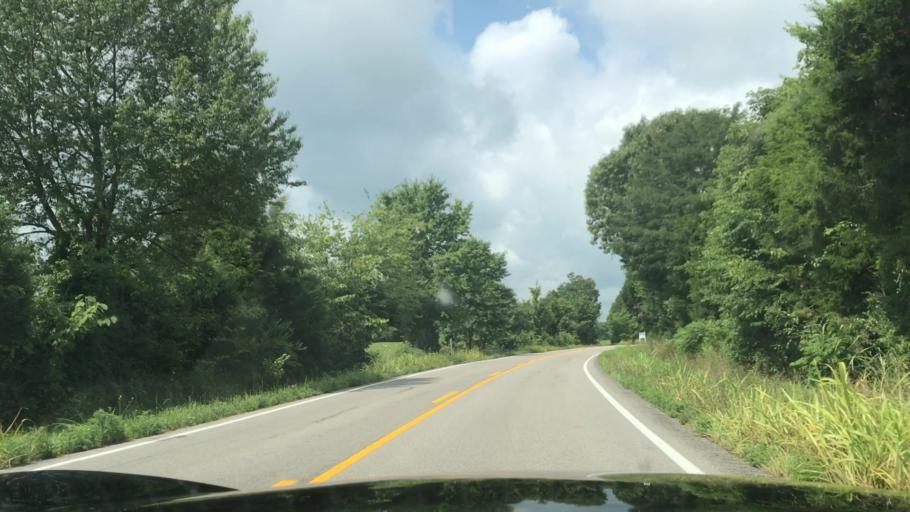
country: US
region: Kentucky
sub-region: Muhlenberg County
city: Central City
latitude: 37.1954
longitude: -86.9880
